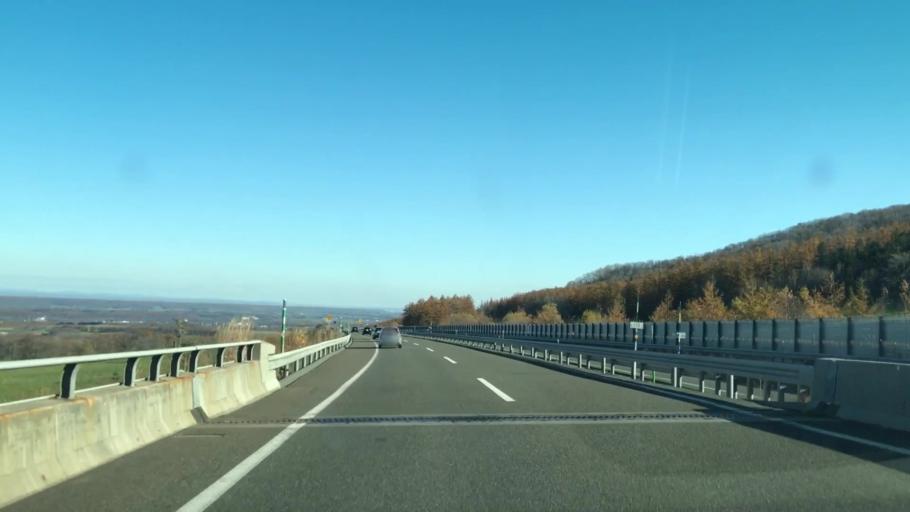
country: JP
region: Hokkaido
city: Otofuke
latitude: 43.0210
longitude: 142.8160
